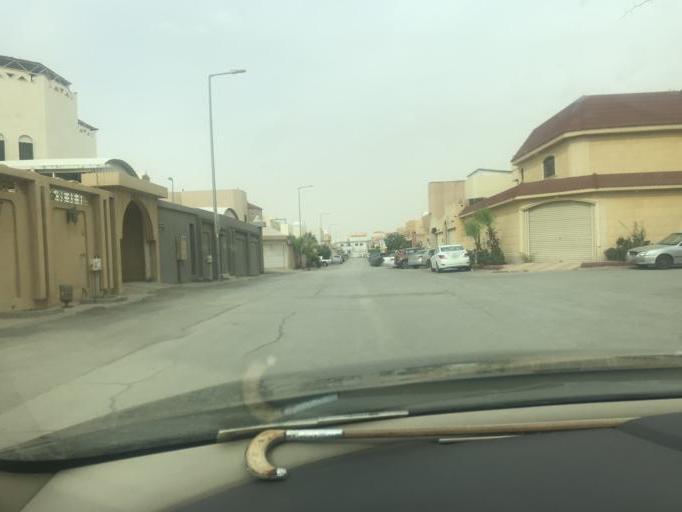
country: SA
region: Ar Riyad
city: Riyadh
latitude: 24.7516
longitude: 46.7620
